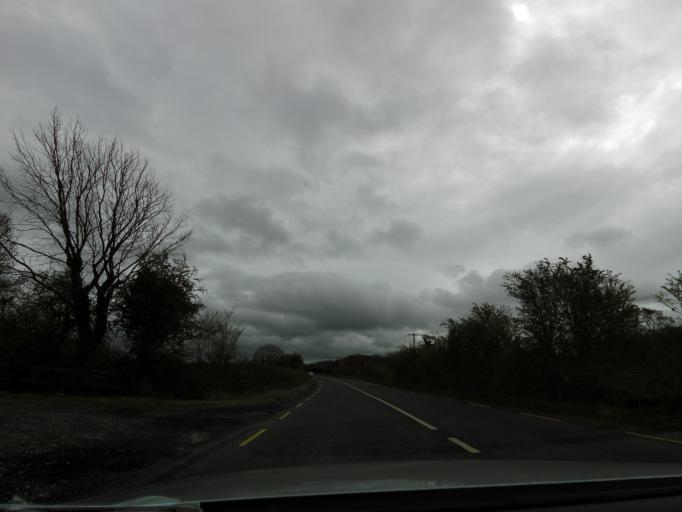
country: IE
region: Leinster
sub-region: Kilkenny
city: Ballyragget
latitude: 52.7277
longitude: -7.3770
